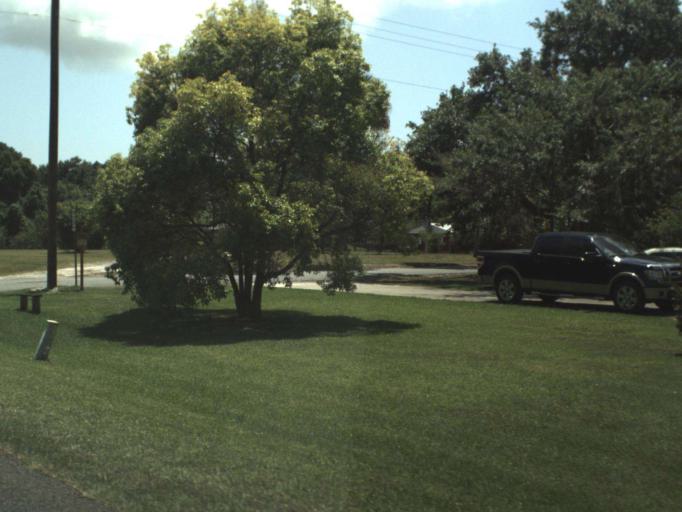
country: US
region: Florida
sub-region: Volusia County
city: Oak Hill
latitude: 28.8440
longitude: -80.8461
